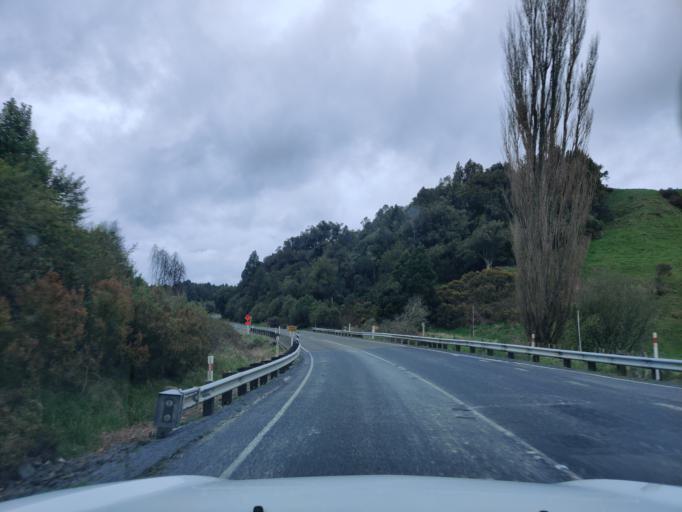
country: NZ
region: Waikato
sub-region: Otorohanga District
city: Otorohanga
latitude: -38.5309
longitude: 175.1776
